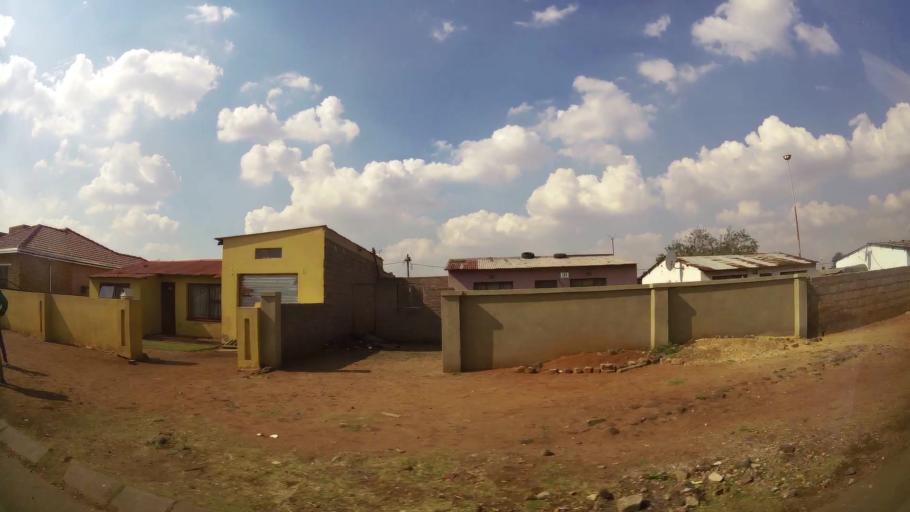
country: ZA
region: Gauteng
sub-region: Ekurhuleni Metropolitan Municipality
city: Germiston
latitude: -26.3385
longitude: 28.1446
